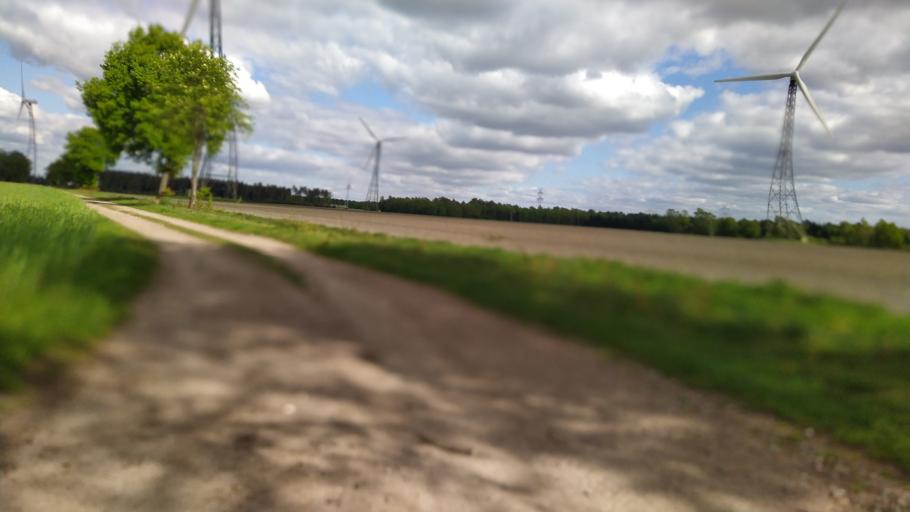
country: DE
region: Lower Saxony
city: Brest
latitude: 53.4351
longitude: 9.3826
